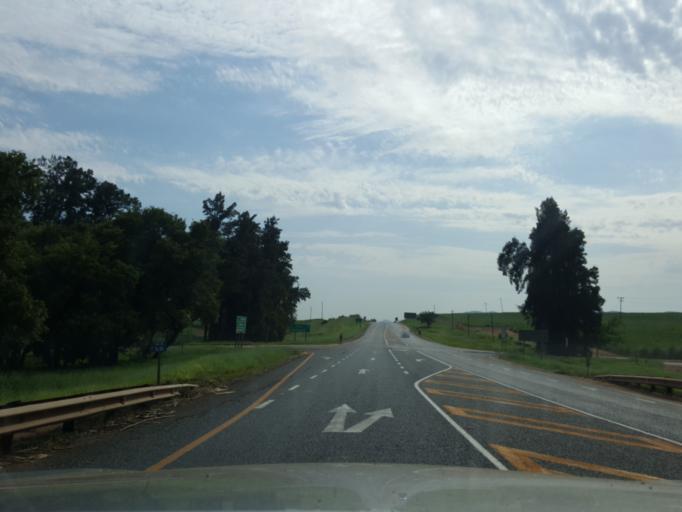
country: SZ
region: Hhohho
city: Ntfonjeni
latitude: -25.5144
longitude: 31.4548
